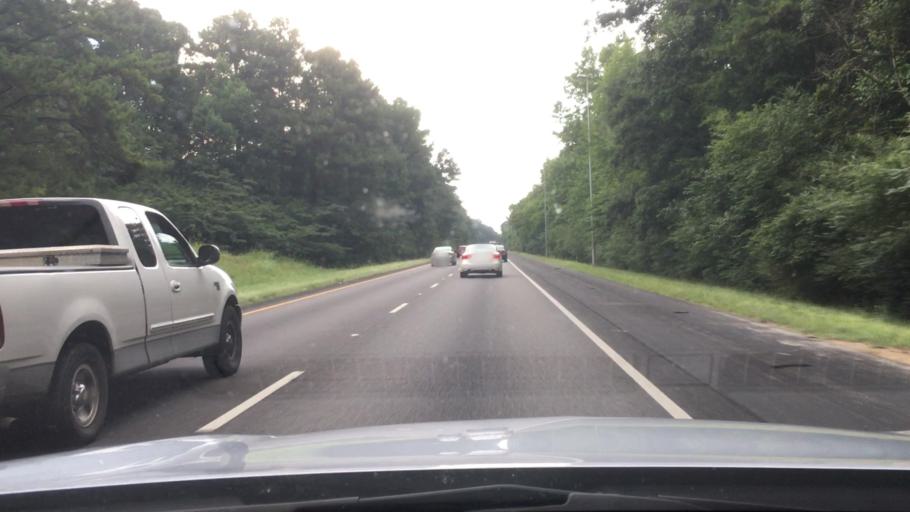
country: US
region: Alabama
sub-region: Jefferson County
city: Trussville
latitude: 33.6205
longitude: -86.6347
